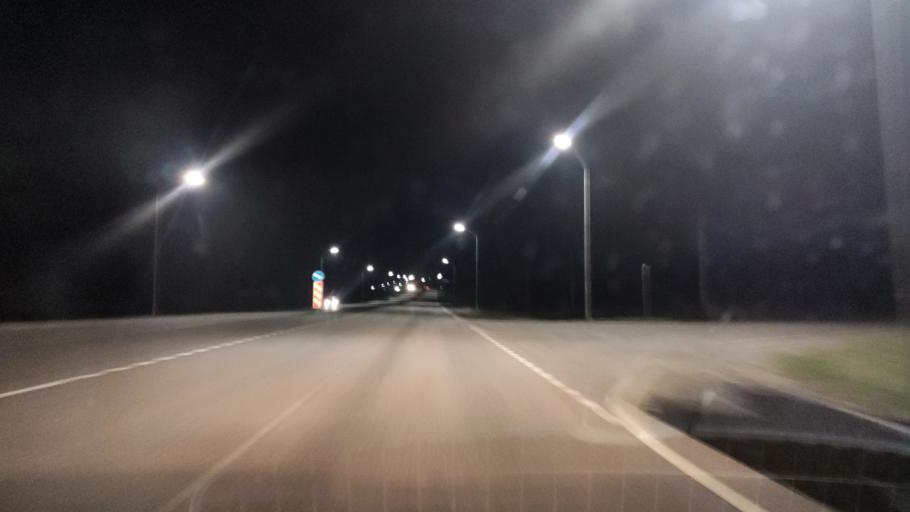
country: RU
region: Belgorod
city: Staryy Oskol
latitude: 51.3898
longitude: 37.8652
